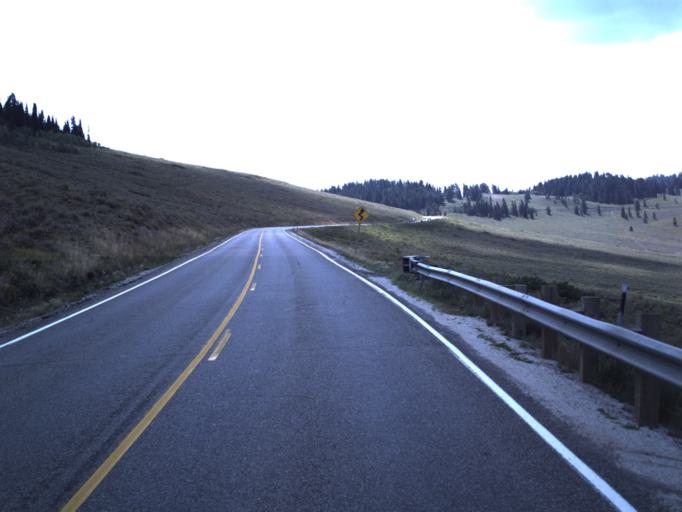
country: US
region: Idaho
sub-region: Bear Lake County
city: Paris
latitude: 41.9331
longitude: -111.4818
